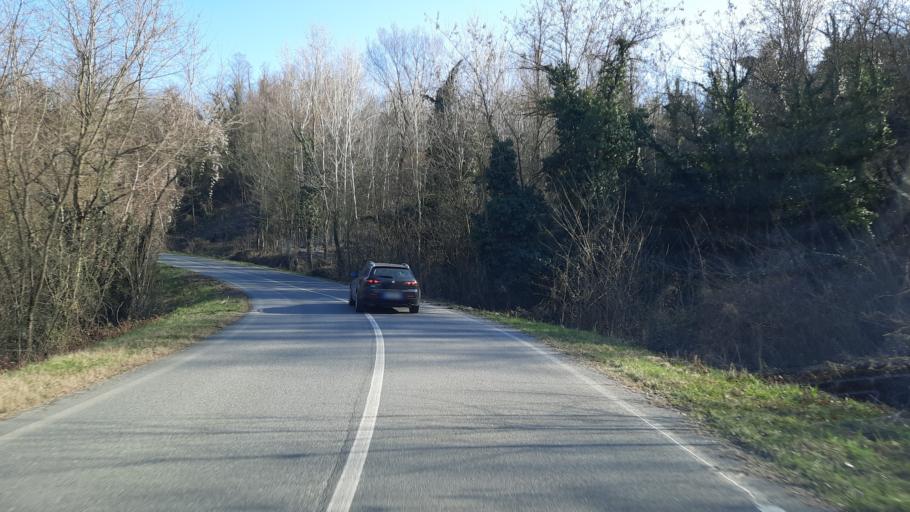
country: IT
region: Piedmont
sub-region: Provincia di Alessandria
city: Camino
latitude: 45.1695
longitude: 8.2839
